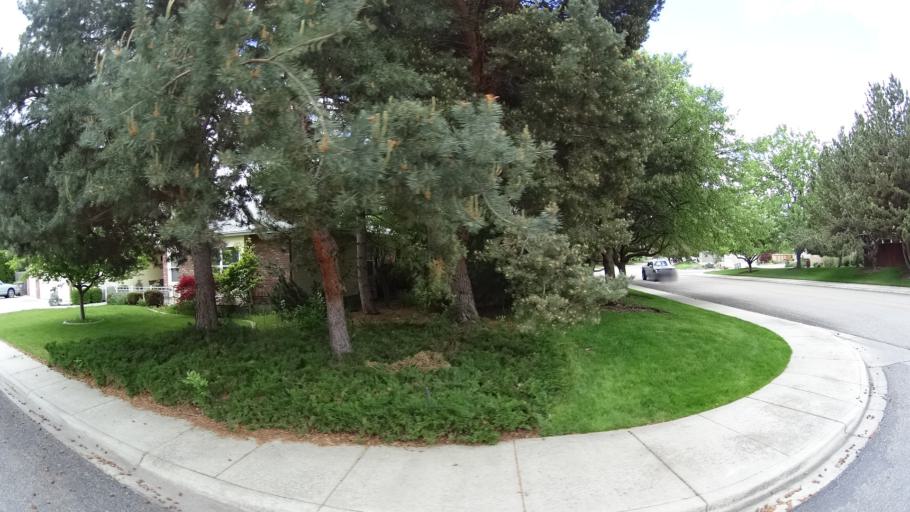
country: US
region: Idaho
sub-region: Ada County
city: Garden City
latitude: 43.6660
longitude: -116.2166
